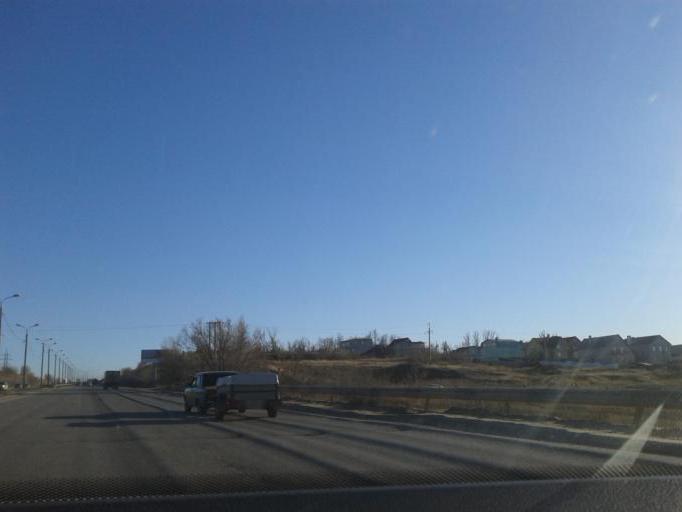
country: RU
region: Volgograd
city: Volgograd
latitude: 48.7123
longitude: 44.4431
